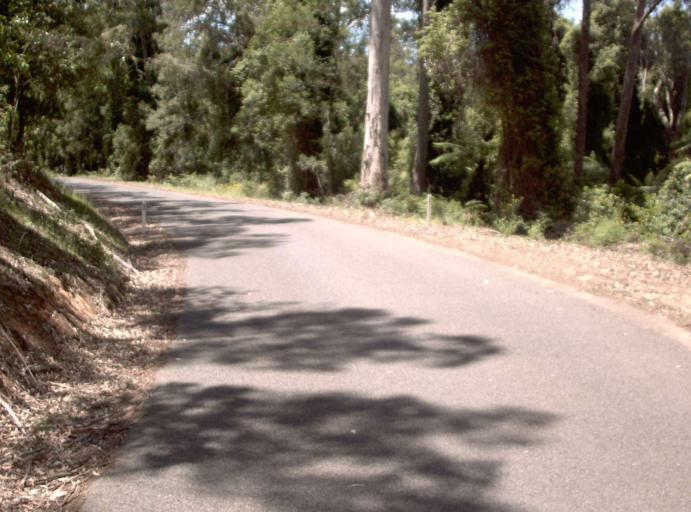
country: AU
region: New South Wales
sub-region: Bombala
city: Bombala
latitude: -37.4703
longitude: 148.9314
